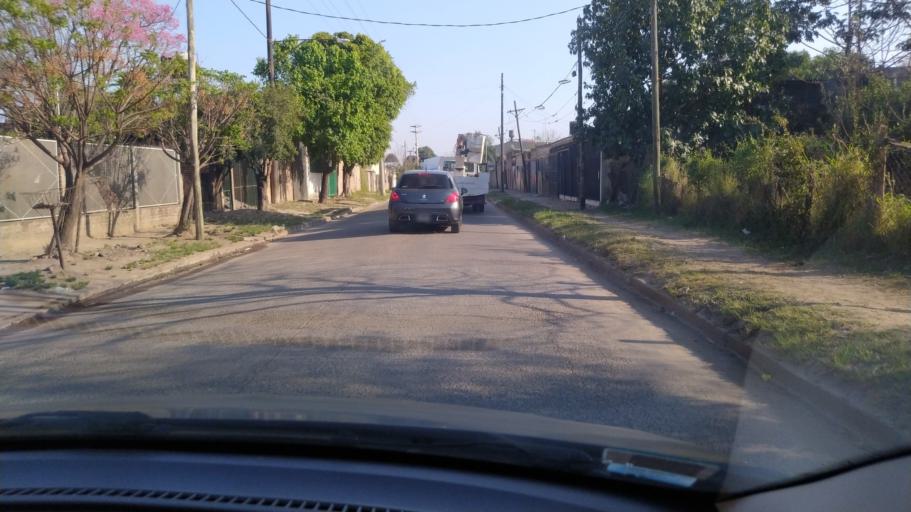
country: AR
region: Corrientes
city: Corrientes
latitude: -27.4933
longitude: -58.8162
